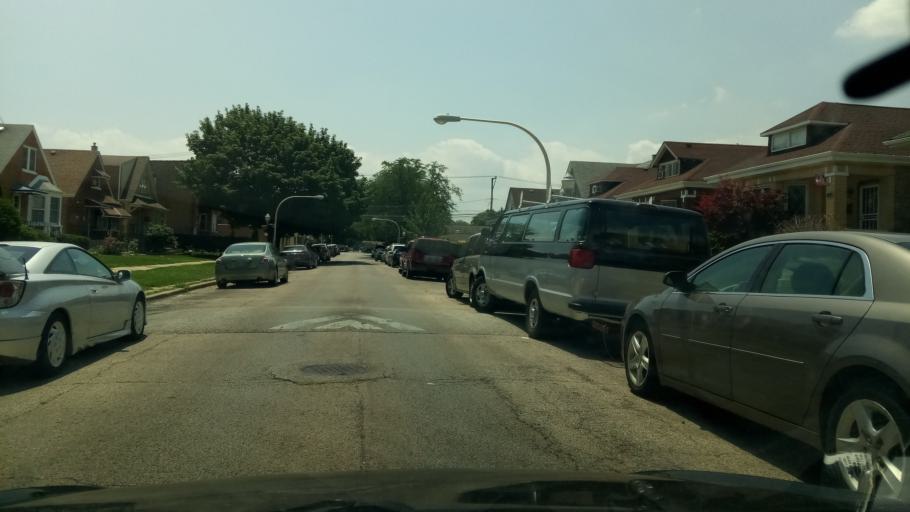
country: US
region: Illinois
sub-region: Cook County
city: Hometown
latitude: 41.7798
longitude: -87.7338
